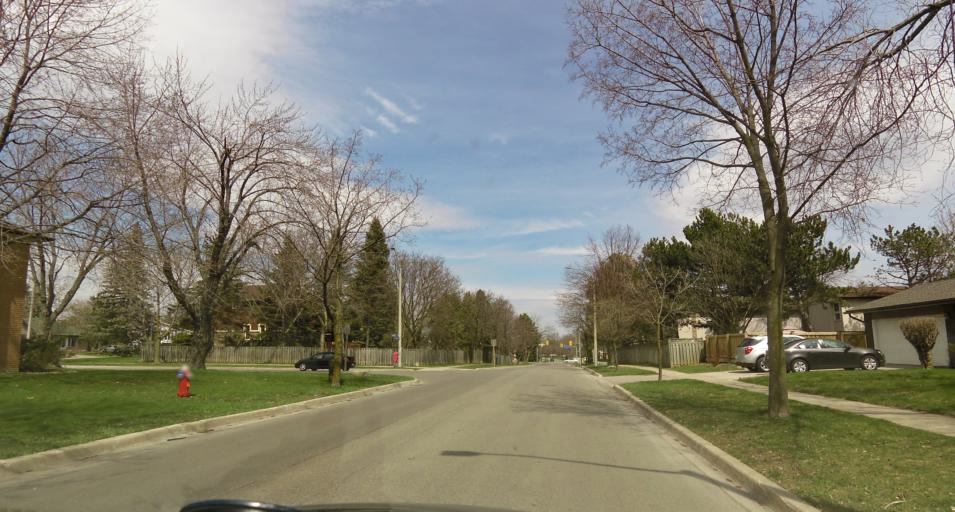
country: CA
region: Ontario
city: Mississauga
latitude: 43.6032
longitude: -79.7223
